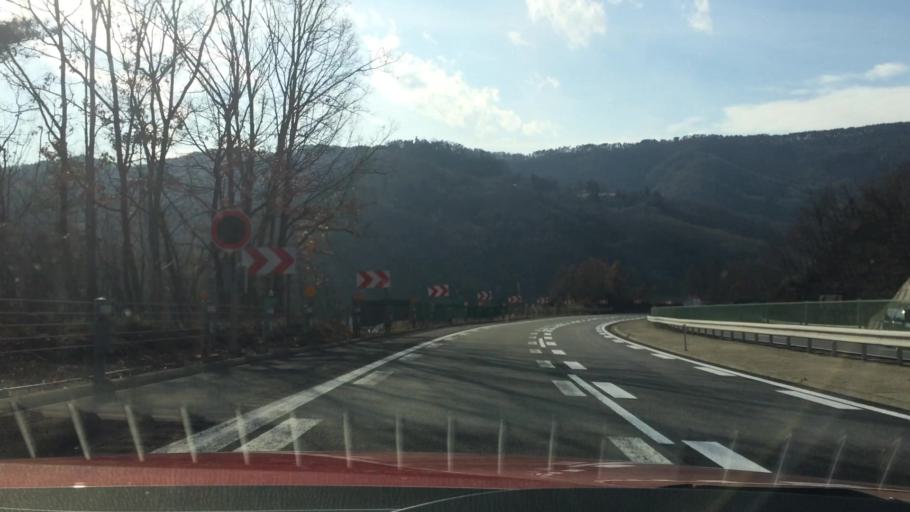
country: JP
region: Nagano
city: Toyoshina
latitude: 36.3456
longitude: 137.9615
